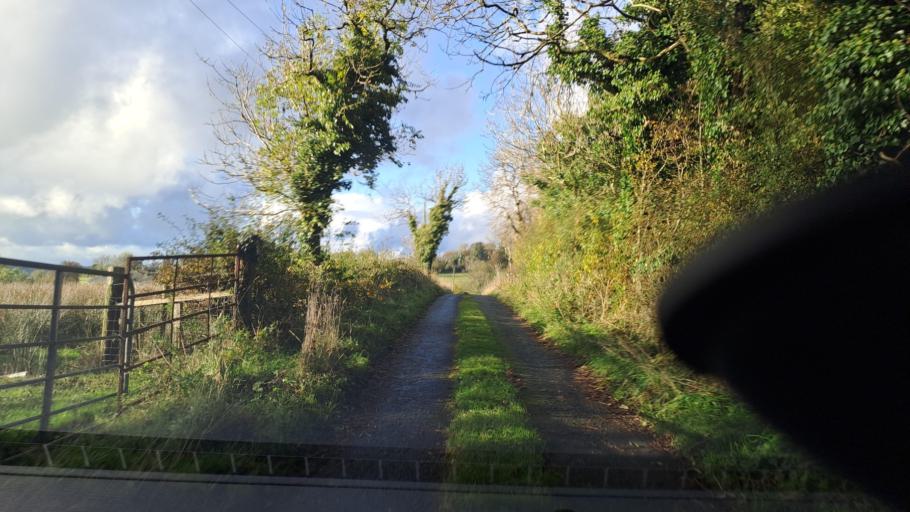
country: IE
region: Ulster
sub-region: An Cabhan
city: Bailieborough
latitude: 53.9370
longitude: -6.9515
